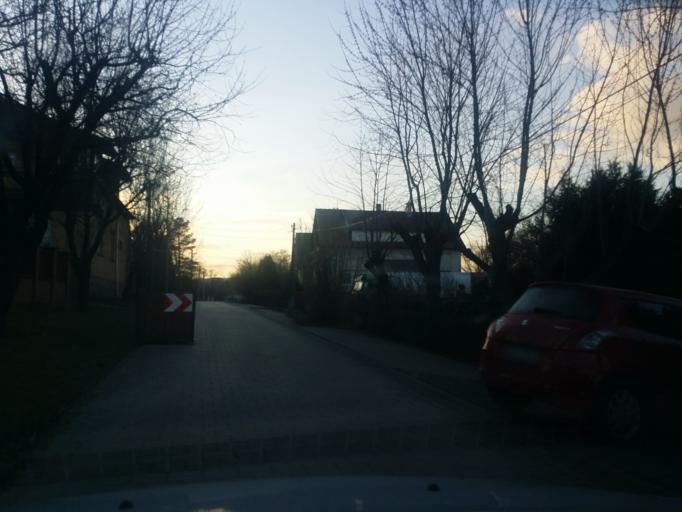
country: HU
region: Pest
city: Pilisvorosvar
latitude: 47.6174
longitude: 18.9195
